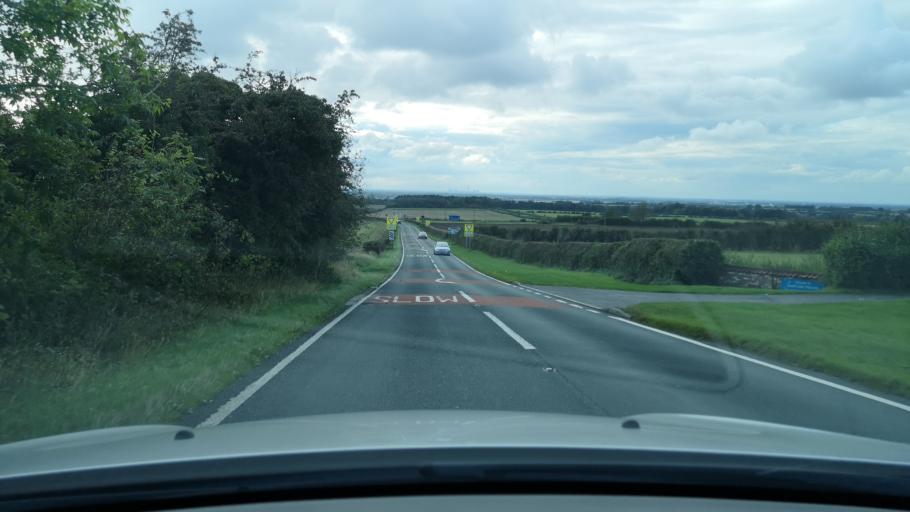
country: GB
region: England
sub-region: East Riding of Yorkshire
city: South Cave
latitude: 53.7950
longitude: -0.6074
